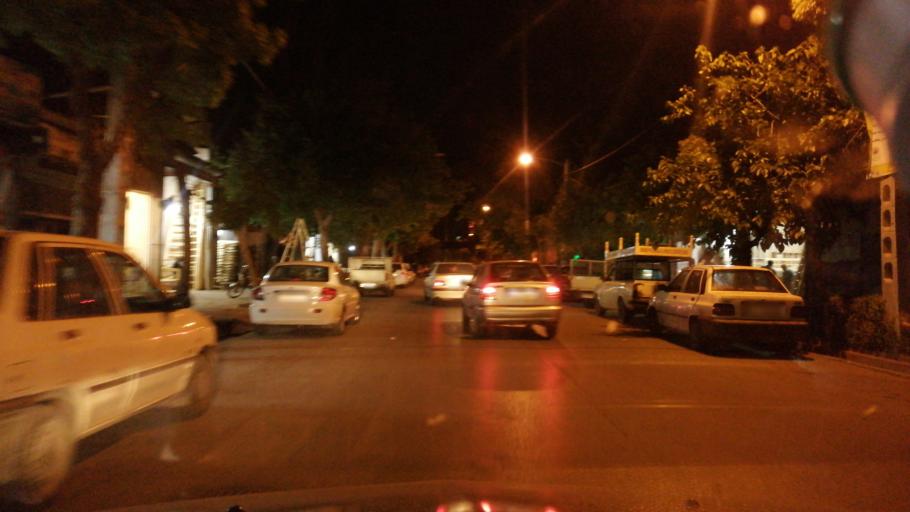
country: IR
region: Razavi Khorasan
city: Mashhad
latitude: 36.3041
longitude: 59.6000
